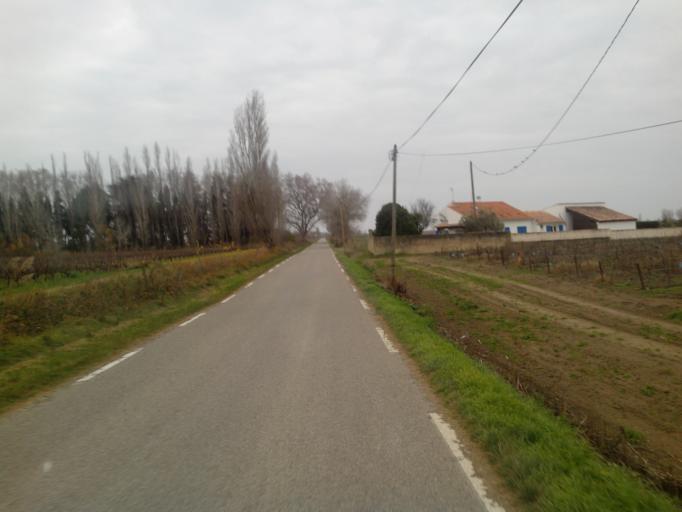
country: FR
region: Languedoc-Roussillon
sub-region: Departement du Gard
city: Vauvert
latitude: 43.5769
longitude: 4.3326
